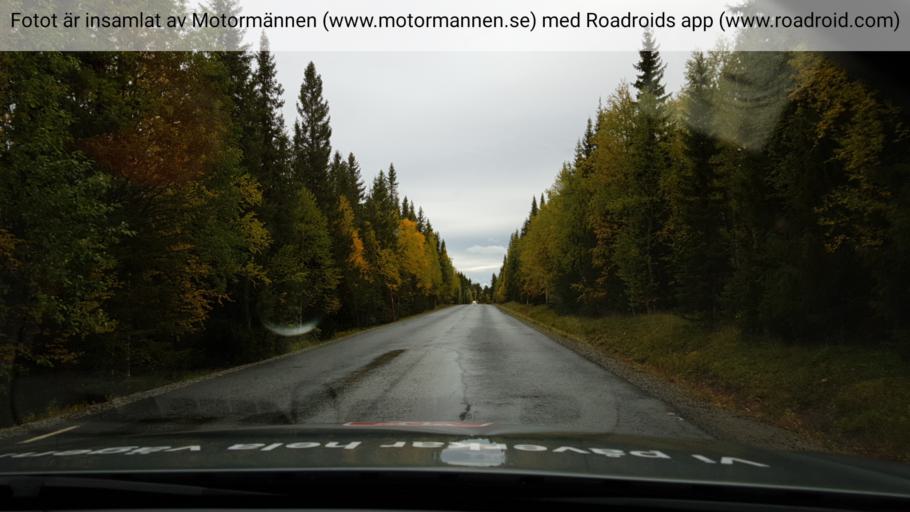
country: SE
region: Vaesterbotten
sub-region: Vilhelmina Kommun
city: Sjoberg
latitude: 64.6723
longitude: 16.2944
